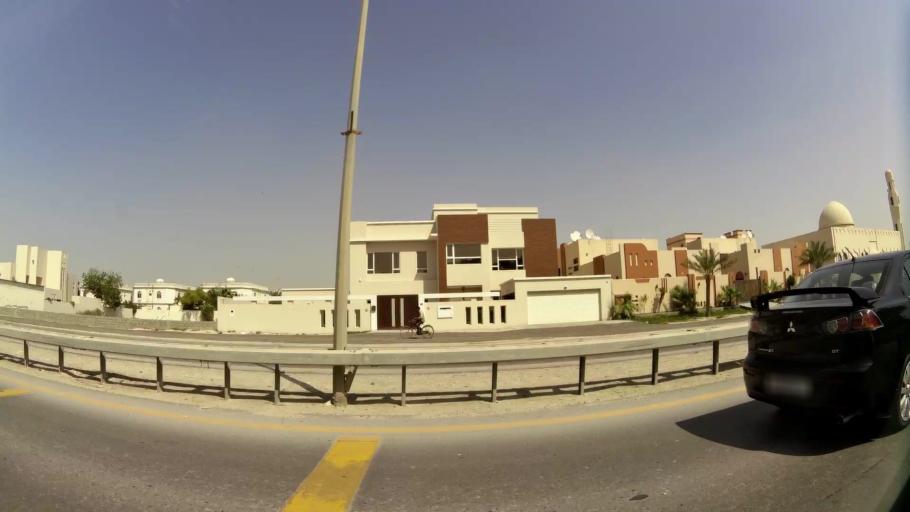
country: BH
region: Manama
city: Jidd Hafs
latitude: 26.1979
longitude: 50.4606
